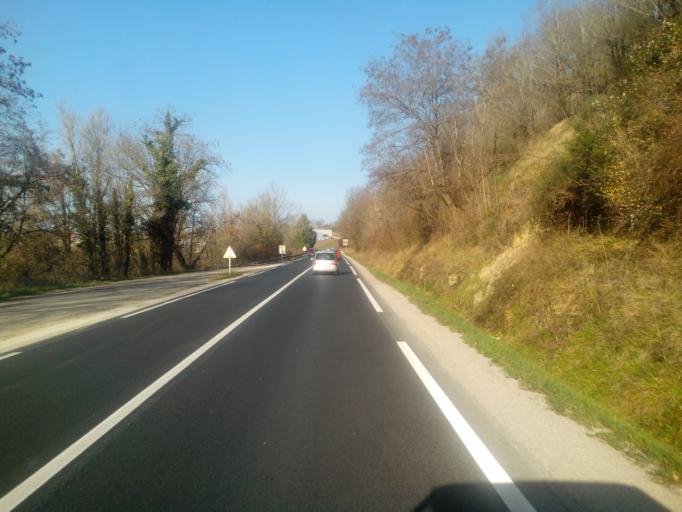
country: FR
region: Midi-Pyrenees
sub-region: Departement de l'Aveyron
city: Capdenac-Gare
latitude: 44.5864
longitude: 2.0659
